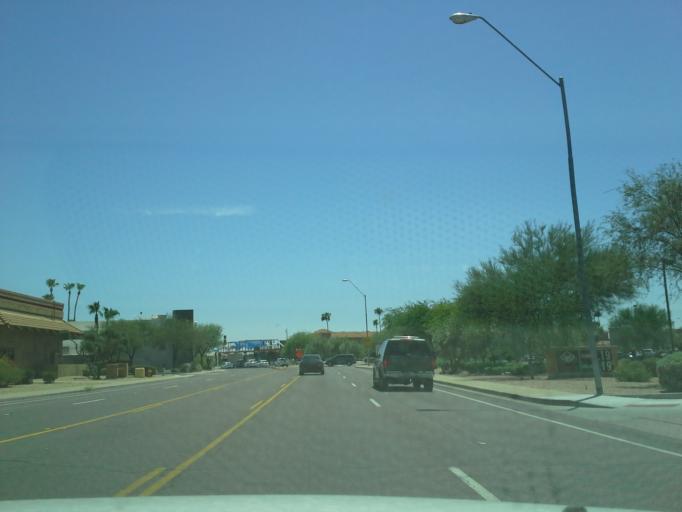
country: US
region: Arizona
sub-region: Maricopa County
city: Scottsdale
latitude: 33.5706
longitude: -111.8872
